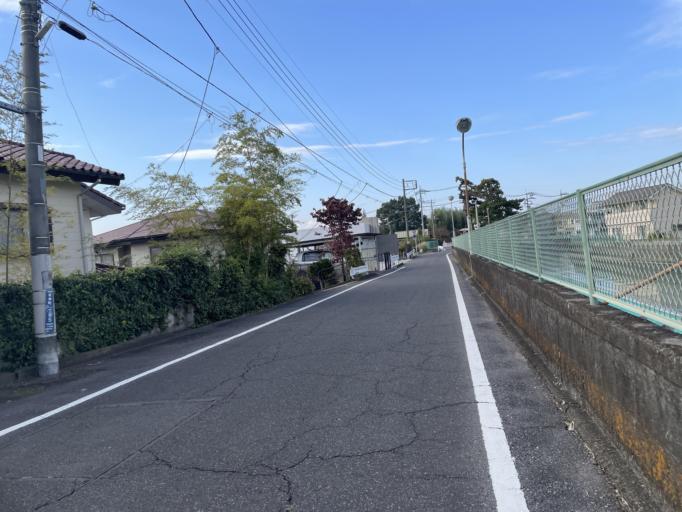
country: JP
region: Gunma
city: Maebashi-shi
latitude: 36.3979
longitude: 139.0605
